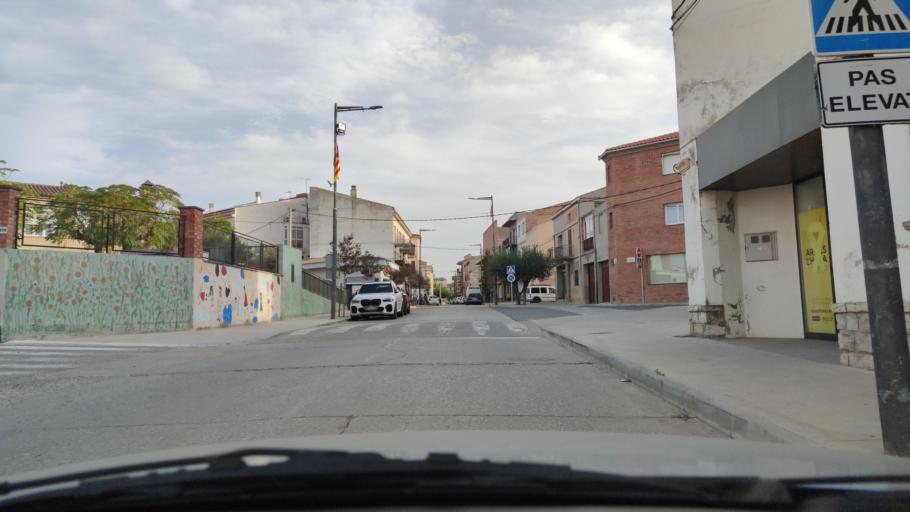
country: ES
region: Catalonia
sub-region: Provincia de Lleida
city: Anglesola
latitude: 41.6567
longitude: 1.0828
